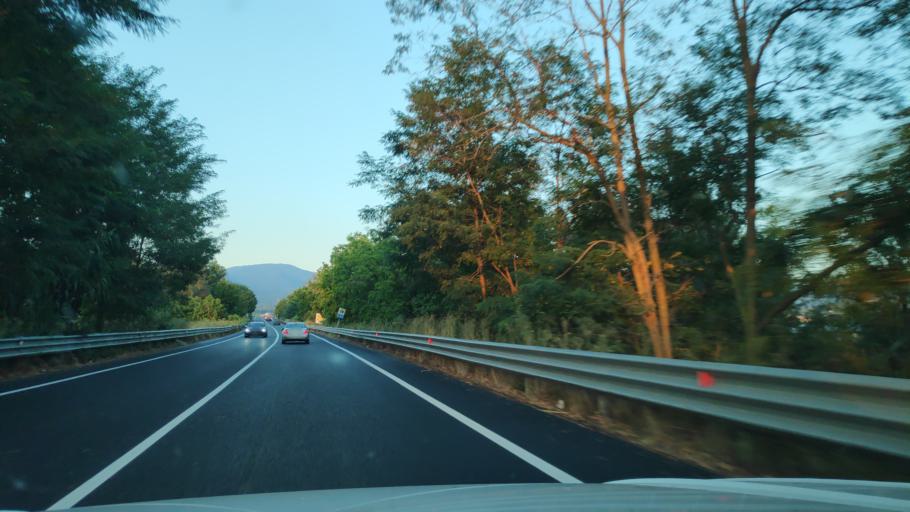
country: IT
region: Calabria
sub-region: Provincia di Reggio Calabria
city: Cinque Frondi
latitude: 38.4174
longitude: 16.0759
